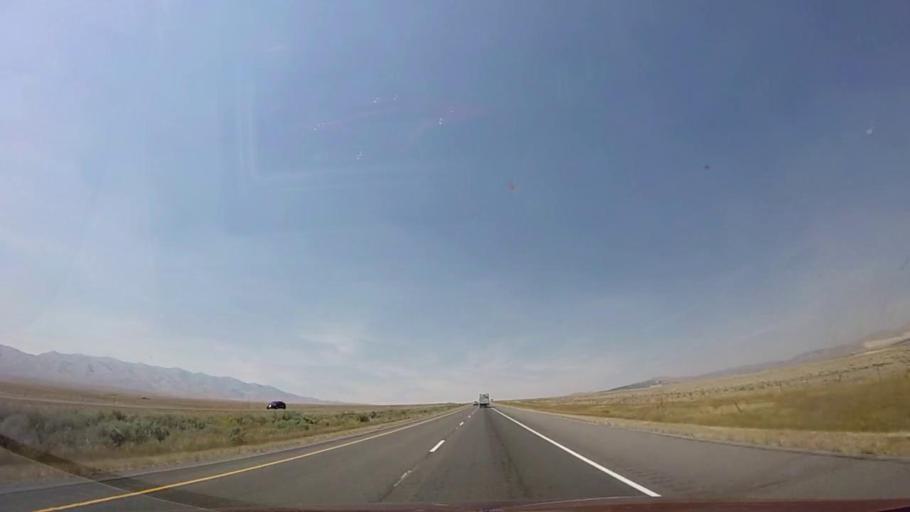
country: US
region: Idaho
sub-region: Power County
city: American Falls
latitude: 42.1185
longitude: -112.9560
